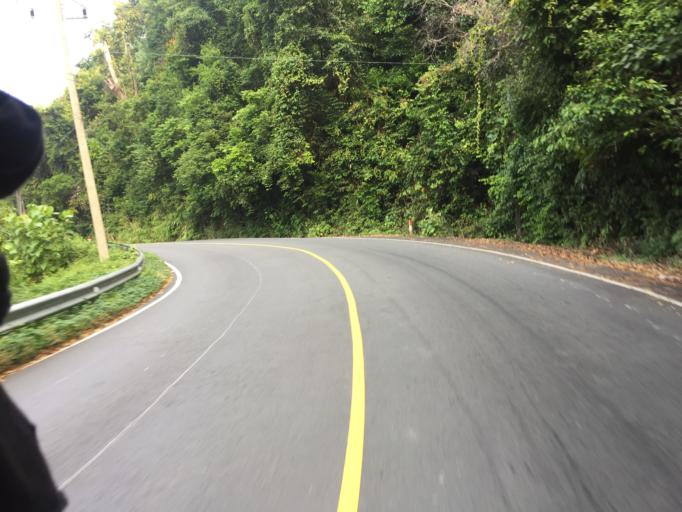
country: TH
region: Trat
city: Laem Ngop
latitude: 12.1195
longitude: 102.2686
